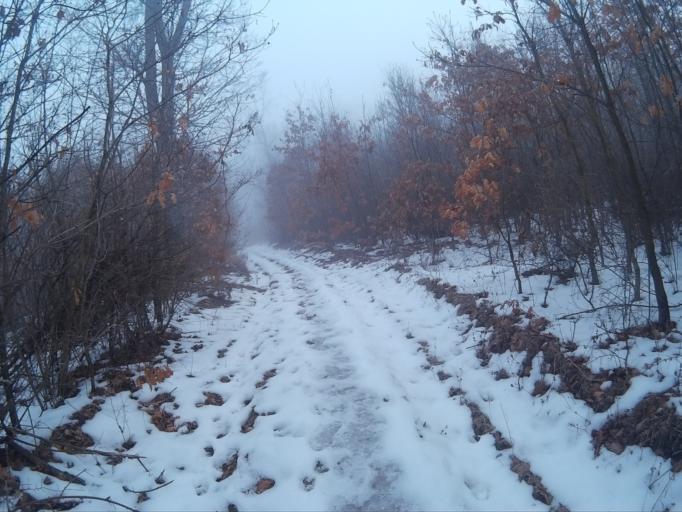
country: HU
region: Nograd
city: Matraverebely
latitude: 47.9893
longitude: 19.7623
